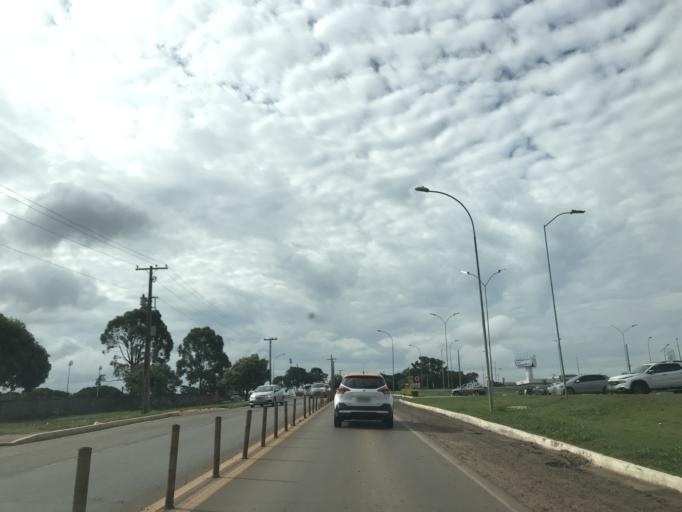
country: BR
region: Federal District
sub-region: Brasilia
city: Brasilia
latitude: -15.6561
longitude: -47.7819
